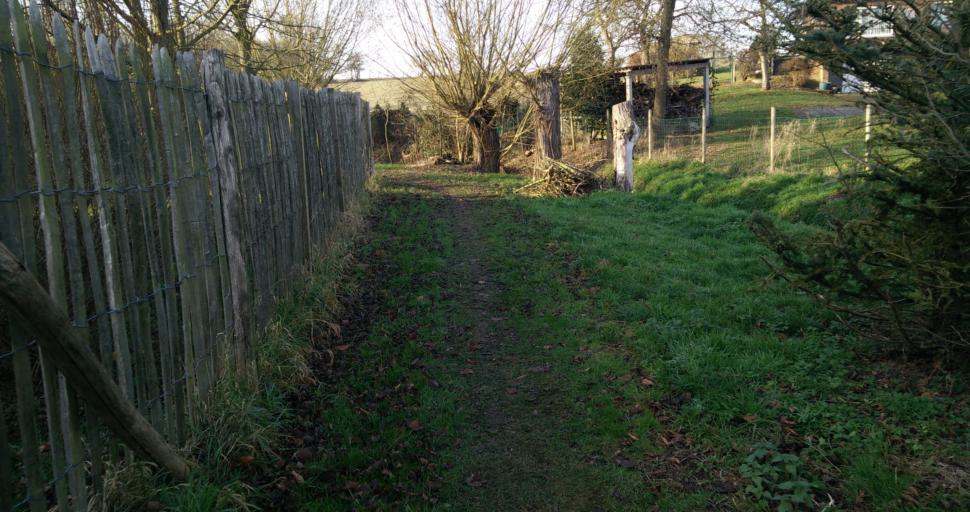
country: BE
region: Flanders
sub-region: Provincie Vlaams-Brabant
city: Halle
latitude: 50.7501
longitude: 4.2303
